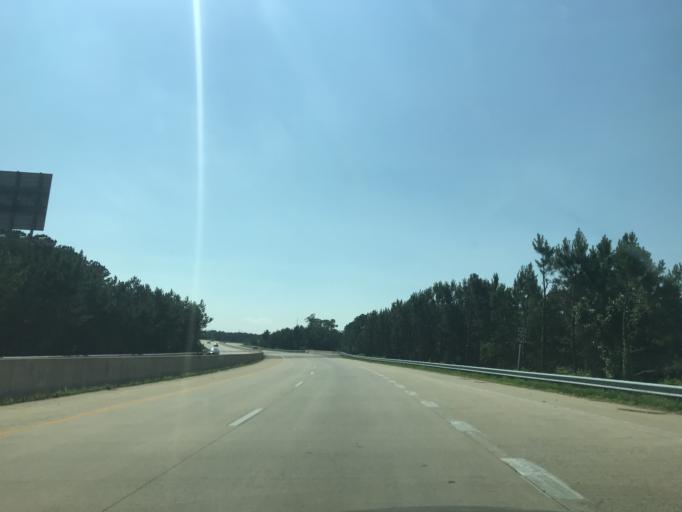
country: US
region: Maryland
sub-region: Wicomico County
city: Salisbury
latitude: 38.4021
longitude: -75.5766
